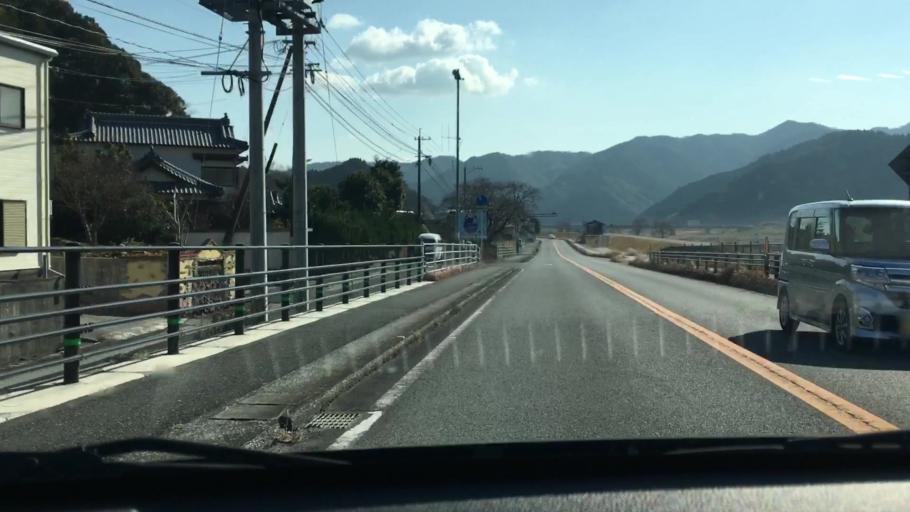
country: JP
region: Oita
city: Saiki
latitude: 32.9618
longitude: 131.8392
